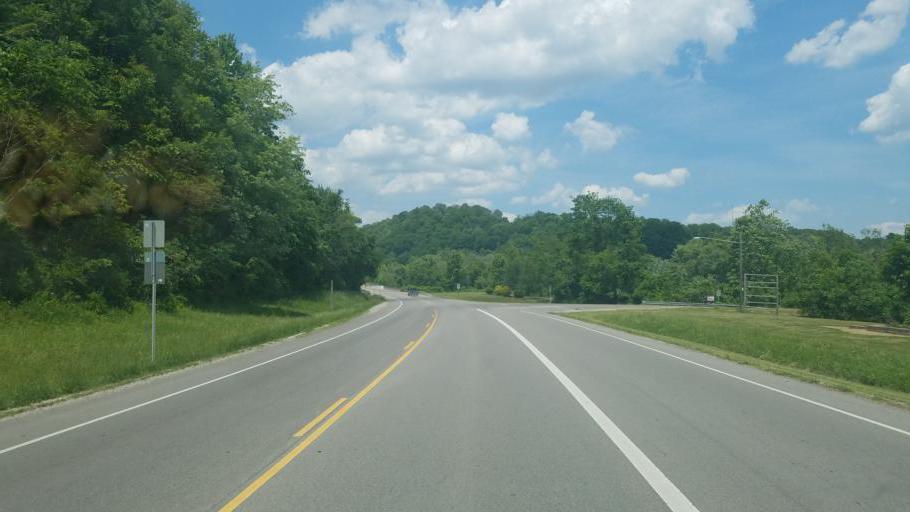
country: US
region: Ohio
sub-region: Meigs County
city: Middleport
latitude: 38.9909
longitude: -82.0771
